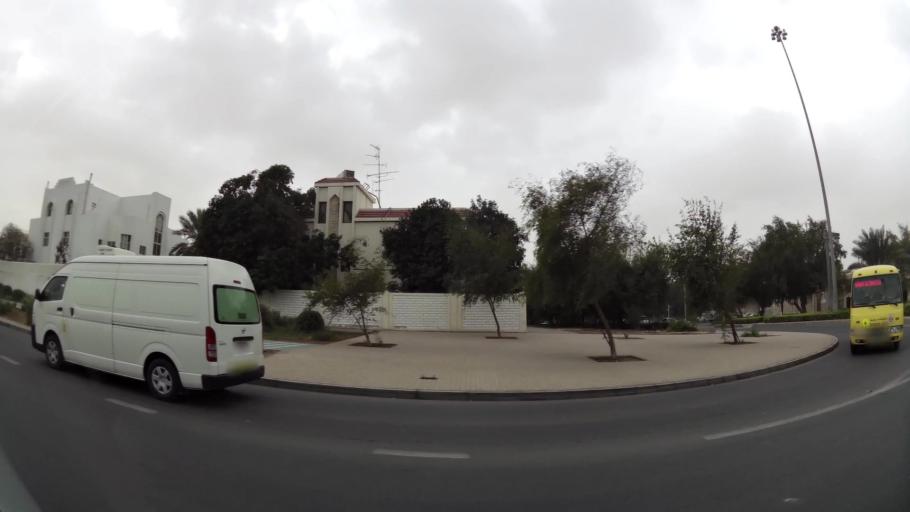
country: AE
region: Abu Dhabi
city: Abu Dhabi
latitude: 24.4442
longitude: 54.4198
